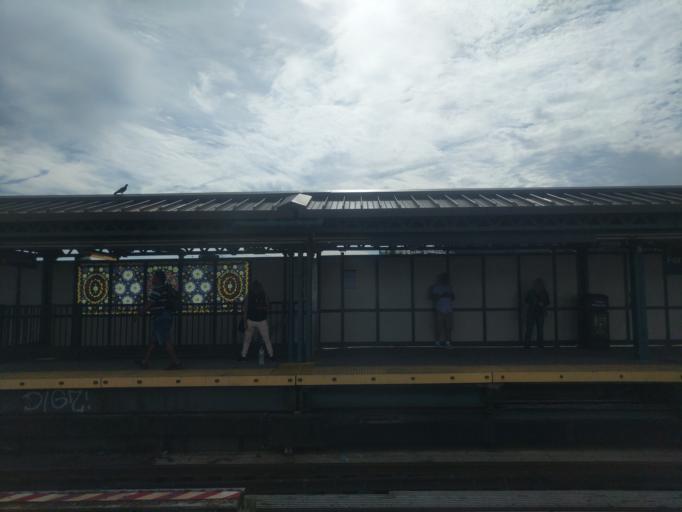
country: US
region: New York
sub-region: Kings County
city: Bensonhurst
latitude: 40.6411
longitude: -73.9943
